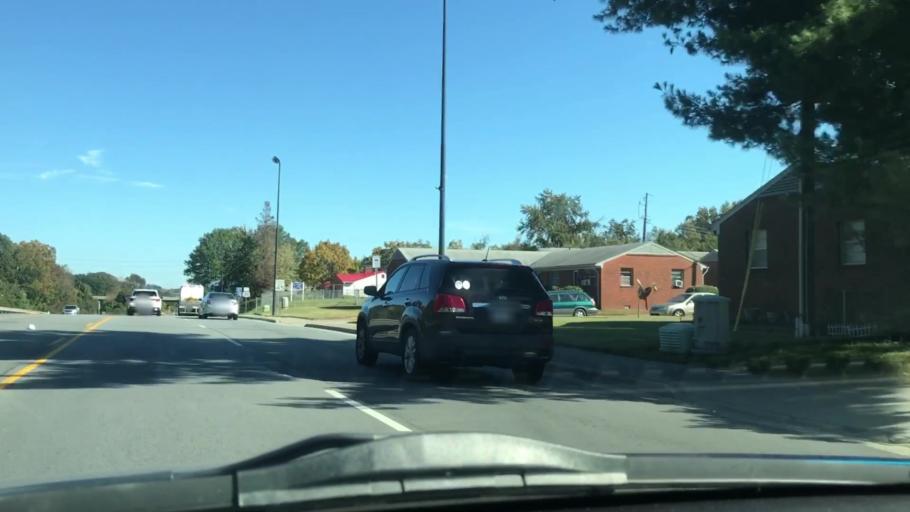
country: US
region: North Carolina
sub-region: Guilford County
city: High Point
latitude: 35.9663
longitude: -79.9809
